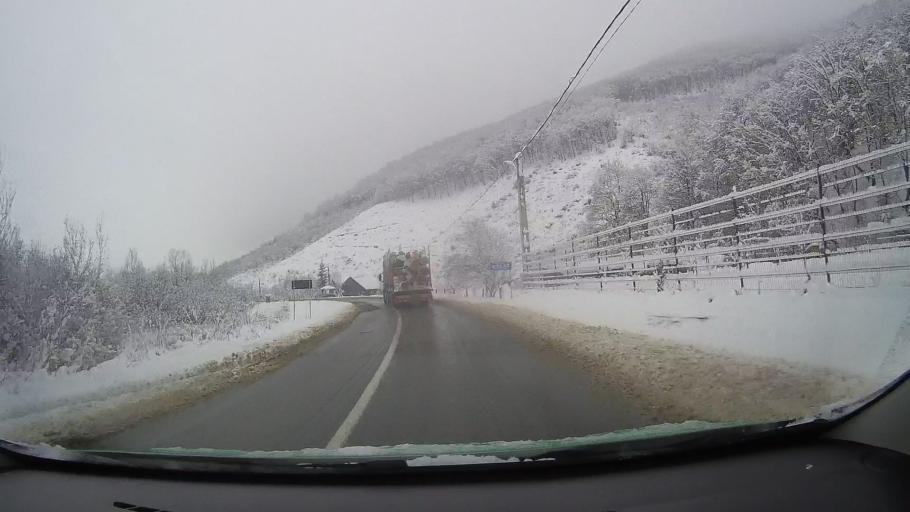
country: RO
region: Sibiu
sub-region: Comuna Orlat
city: Orlat
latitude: 45.7601
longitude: 23.9406
